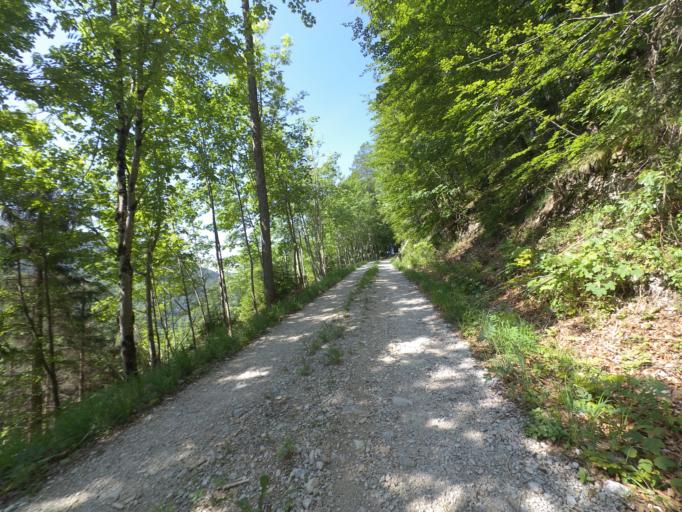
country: AT
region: Salzburg
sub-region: Politischer Bezirk Salzburg-Umgebung
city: Koppl
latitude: 47.7850
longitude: 13.1514
